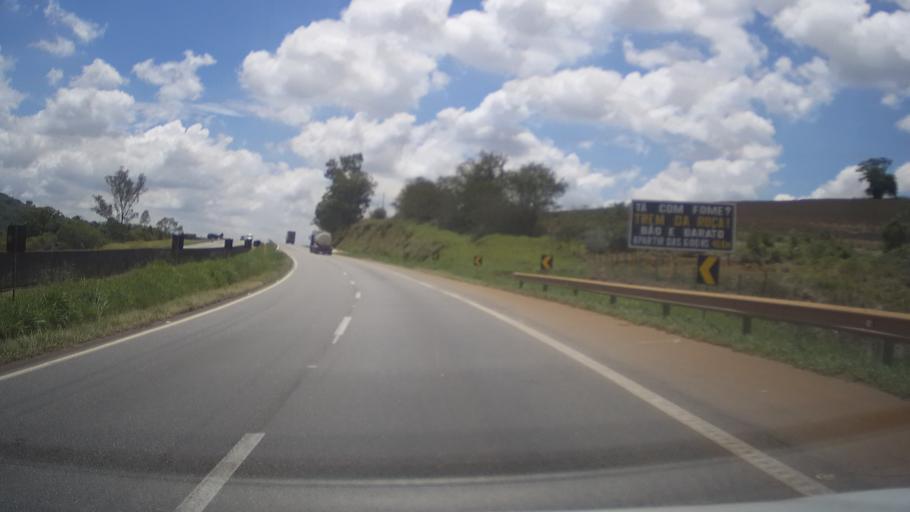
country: BR
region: Minas Gerais
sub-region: Campanha
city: Campanha
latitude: -21.8045
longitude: -45.4743
